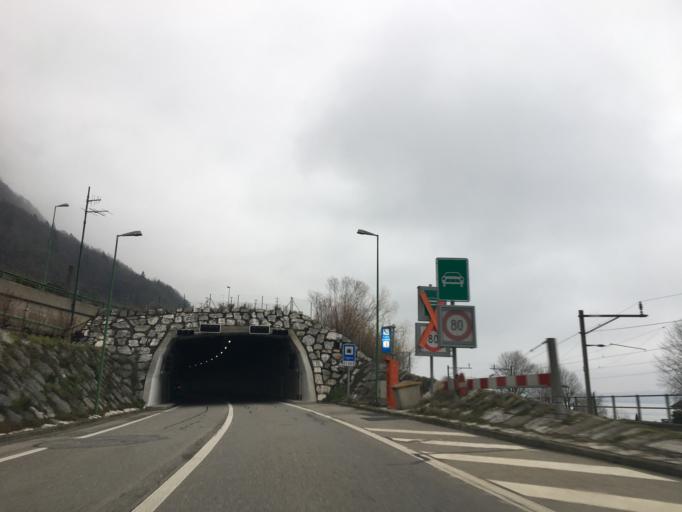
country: CH
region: Bern
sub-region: Jura bernois
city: La Neuveville
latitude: 47.0796
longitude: 7.1239
